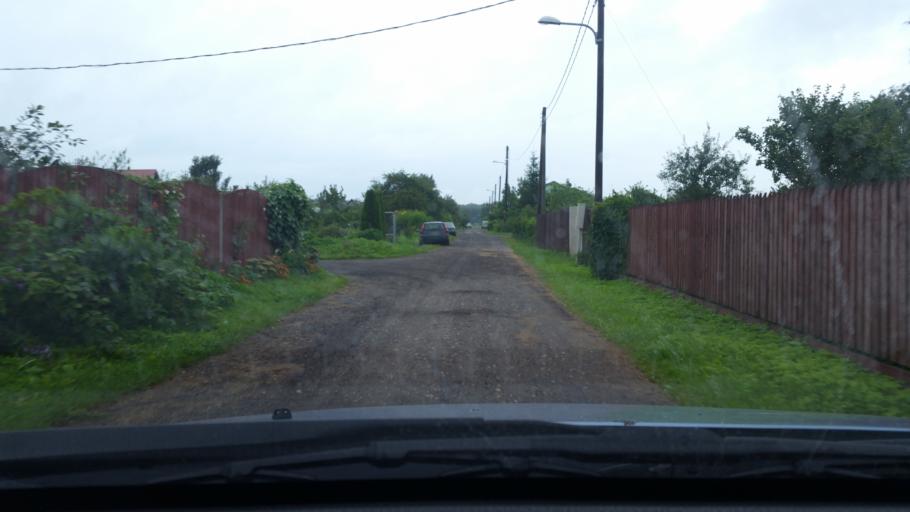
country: LV
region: Riga
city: Bolderaja
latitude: 57.0001
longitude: 24.0354
